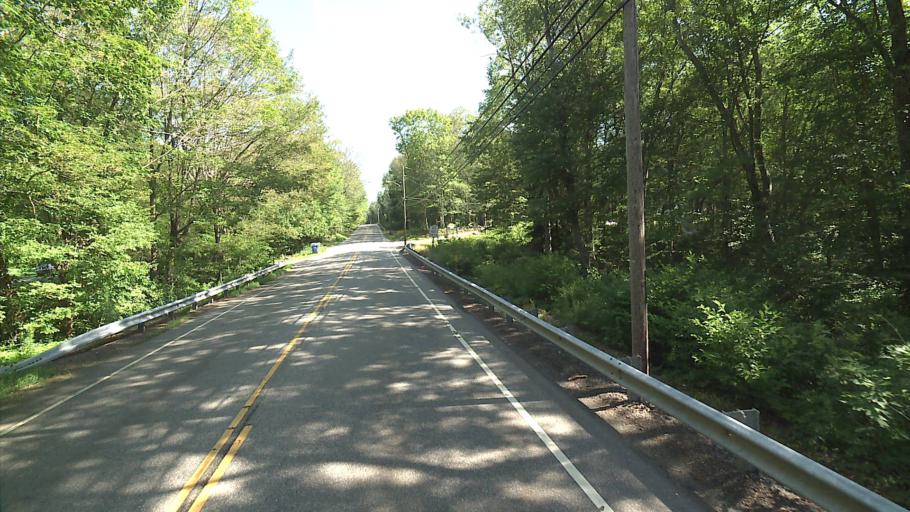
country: US
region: Connecticut
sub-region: New London County
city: Montville Center
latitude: 41.5055
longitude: -72.2031
